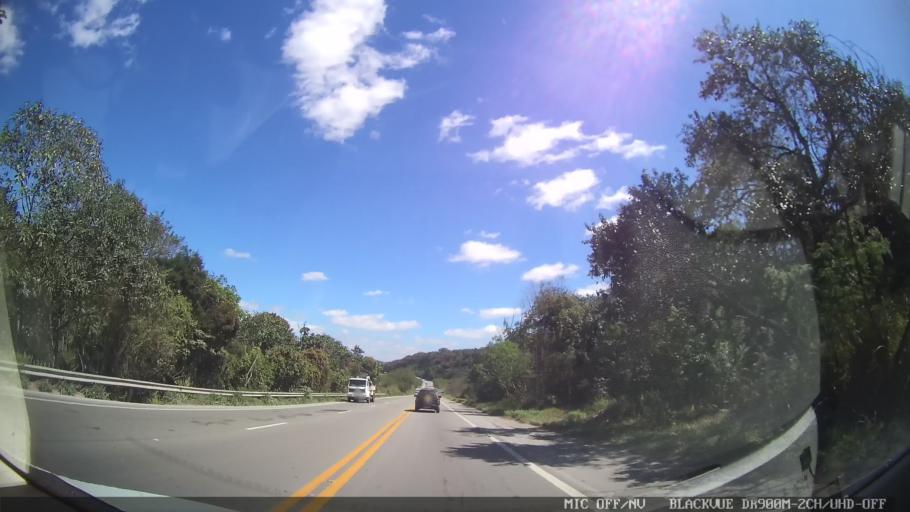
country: BR
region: Sao Paulo
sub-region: Campo Limpo Paulista
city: Campo Limpo Paulista
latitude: -23.1940
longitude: -46.7903
